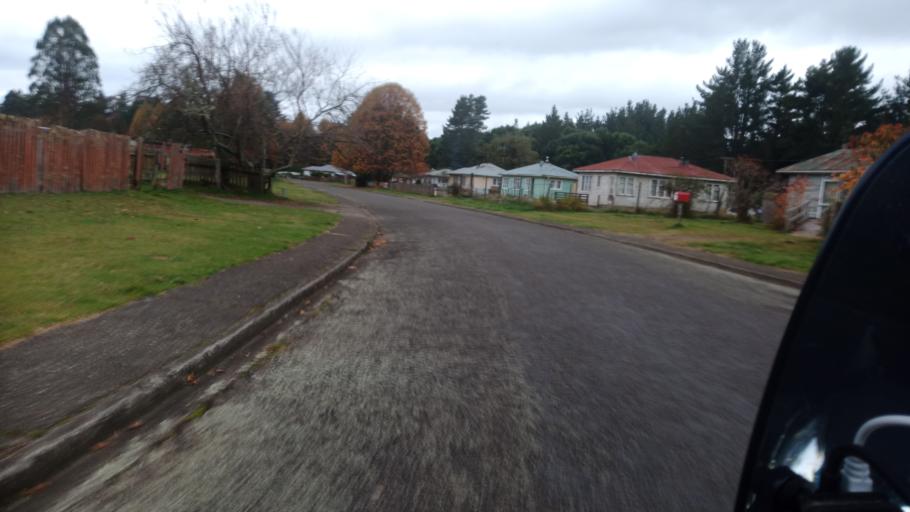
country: NZ
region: Bay of Plenty
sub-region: Whakatane District
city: Murupara
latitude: -38.6413
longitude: 176.7333
